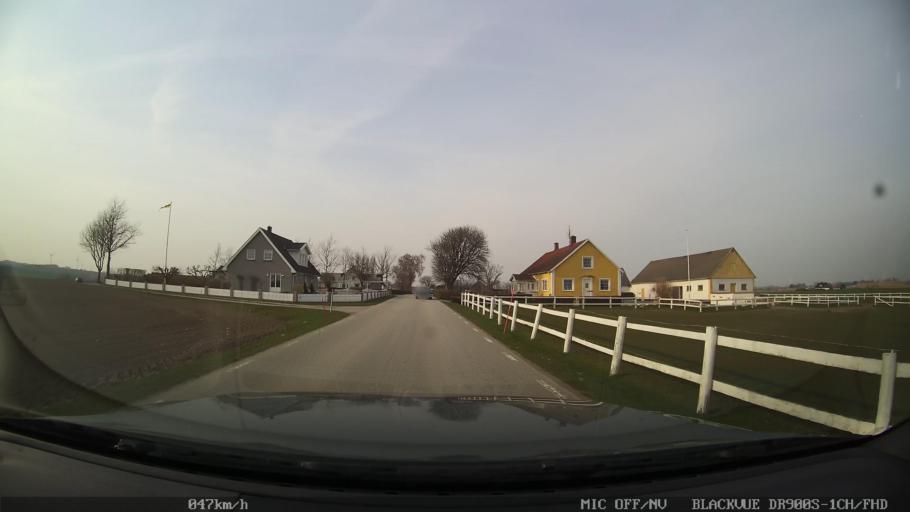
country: SE
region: Skane
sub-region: Ystads Kommun
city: Ystad
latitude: 55.4573
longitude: 13.8281
